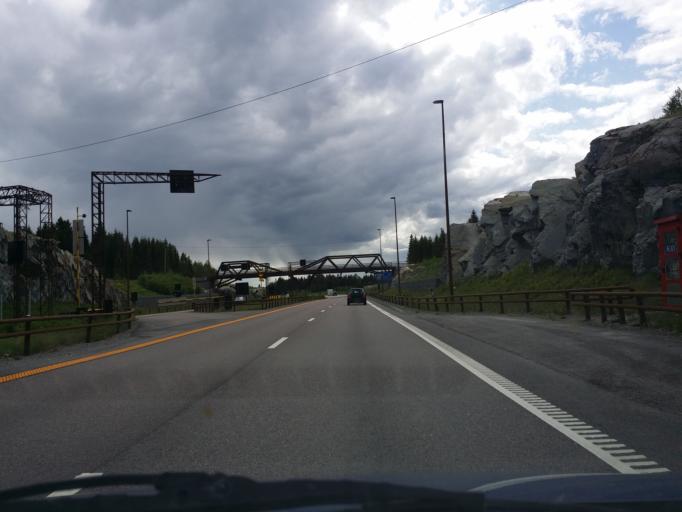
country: NO
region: Akershus
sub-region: Eidsvoll
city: Eidsvoll
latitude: 60.3458
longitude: 11.2080
